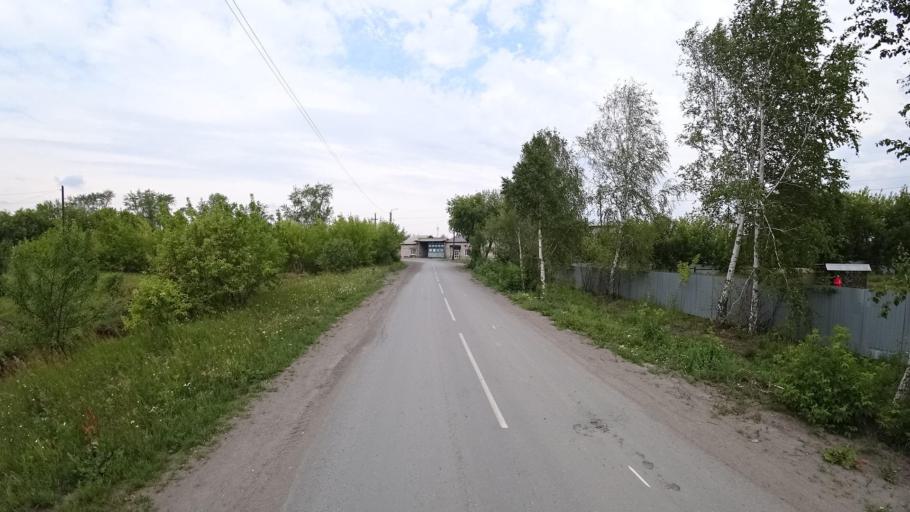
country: RU
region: Sverdlovsk
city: Kamyshlov
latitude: 56.8483
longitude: 62.7354
